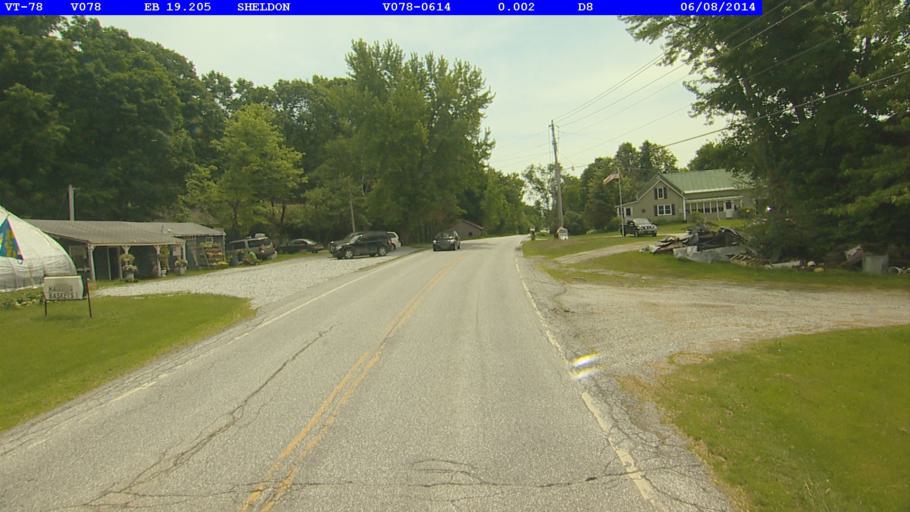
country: US
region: Vermont
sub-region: Franklin County
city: Swanton
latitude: 44.9245
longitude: -72.9677
